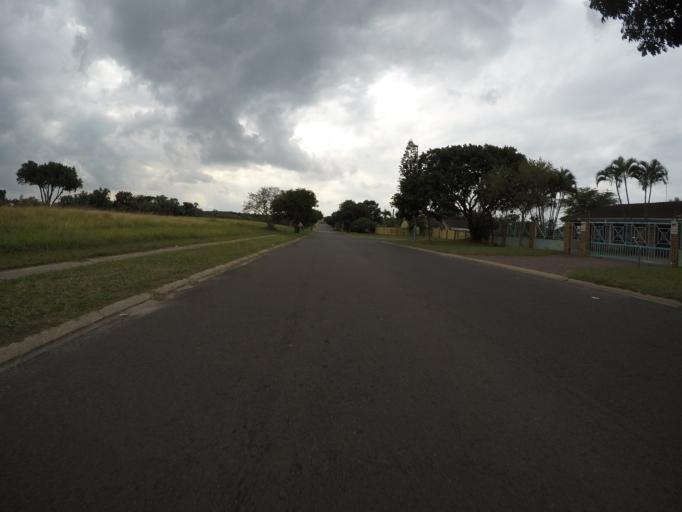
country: ZA
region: KwaZulu-Natal
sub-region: uThungulu District Municipality
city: Richards Bay
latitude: -28.7348
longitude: 32.0499
